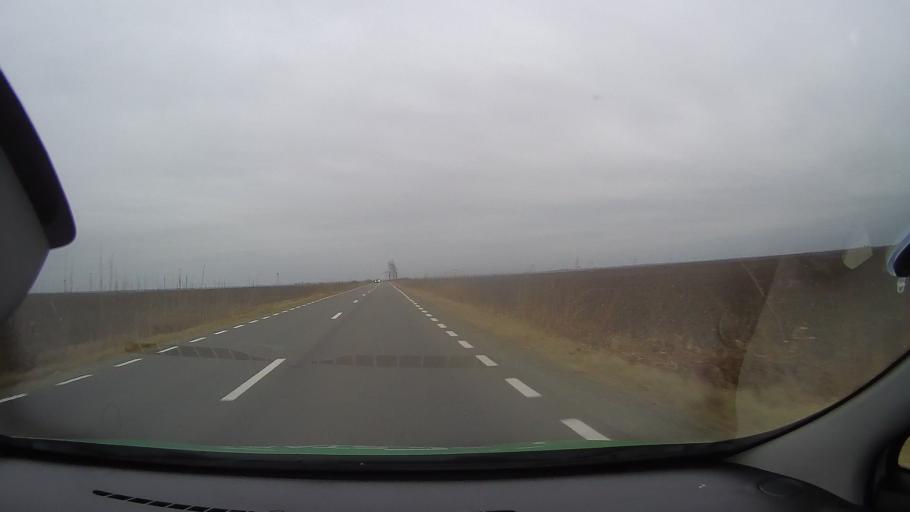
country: RO
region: Ialomita
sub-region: Comuna Gheorghe Lazar
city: Gheorghe Lazar
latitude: 44.6607
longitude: 27.4131
